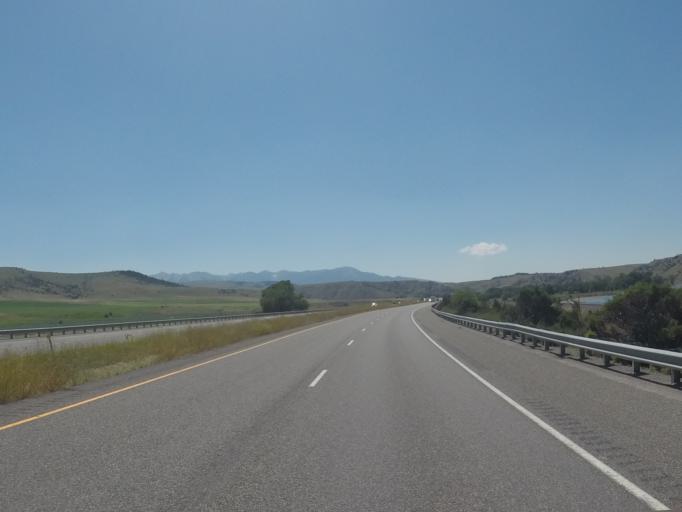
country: US
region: Montana
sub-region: Sweet Grass County
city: Big Timber
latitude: 45.7258
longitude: -110.2413
